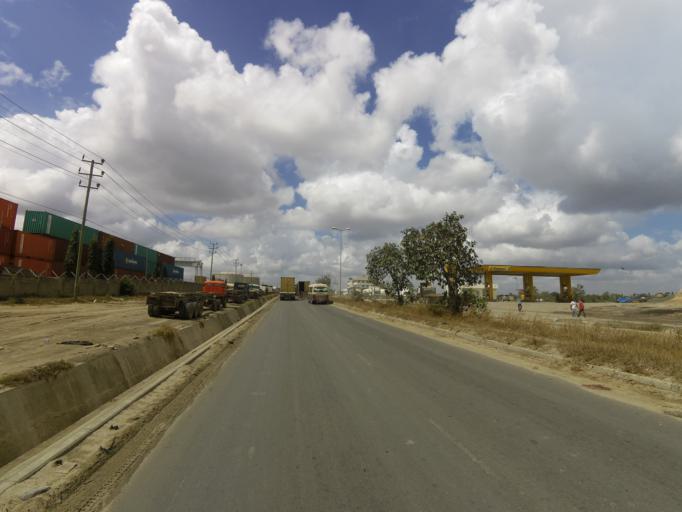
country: TZ
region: Dar es Salaam
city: Dar es Salaam
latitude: -6.8522
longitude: 39.2917
